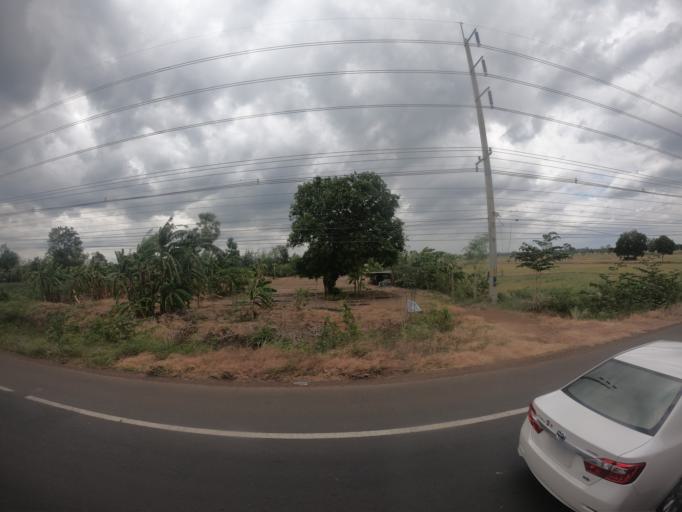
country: TH
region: Buriram
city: Nong Ki
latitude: 14.7007
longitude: 102.4893
